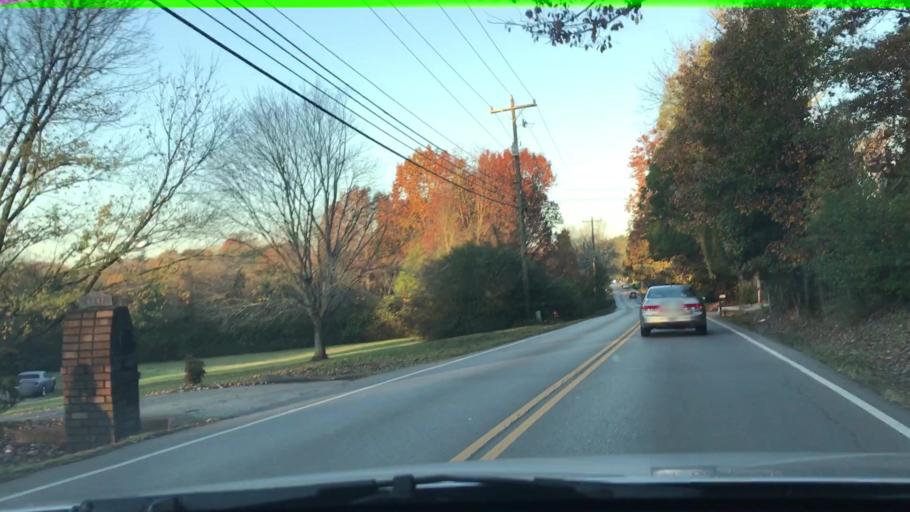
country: US
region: Tennessee
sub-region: Williamson County
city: Brentwood Estates
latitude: 36.0145
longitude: -86.7236
